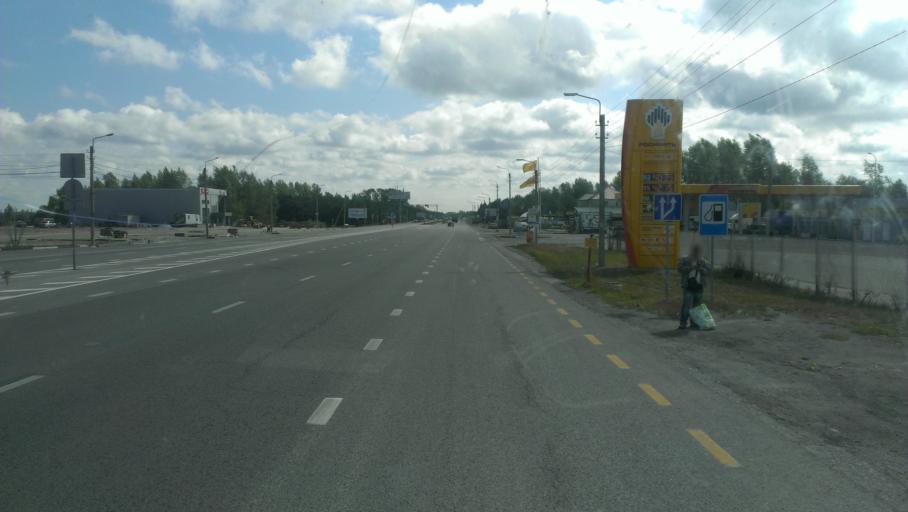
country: RU
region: Altai Krai
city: Zaton
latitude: 53.3152
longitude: 83.8345
